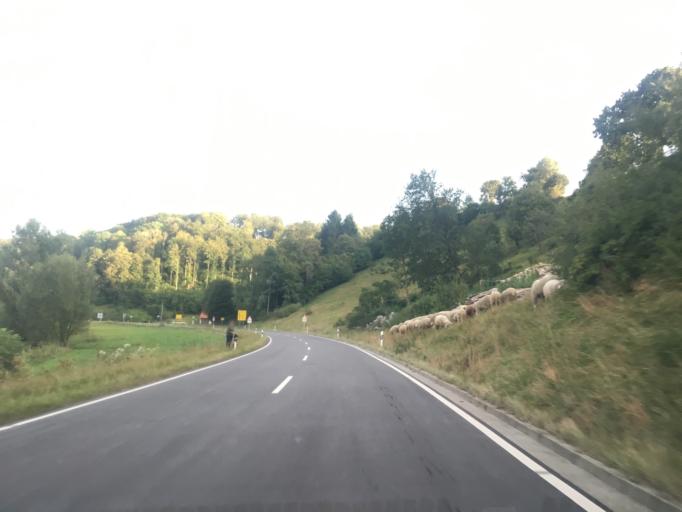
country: DE
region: Baden-Wuerttemberg
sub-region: Tuebingen Region
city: Gomadingen
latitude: 48.3669
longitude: 9.4299
